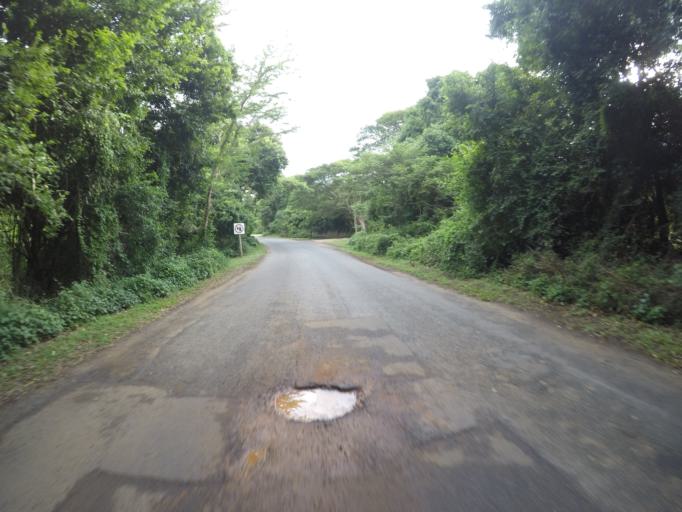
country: ZA
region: KwaZulu-Natal
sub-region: uMkhanyakude District Municipality
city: Mtubatuba
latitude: -28.3863
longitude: 32.4100
